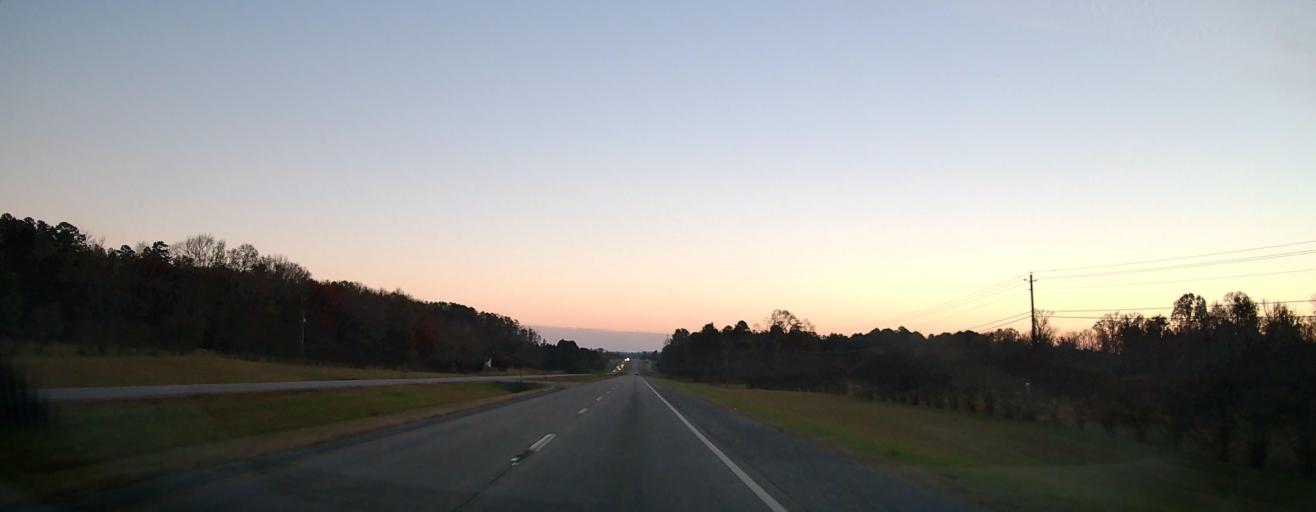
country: US
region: Alabama
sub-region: Calhoun County
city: Alexandria
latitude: 33.8365
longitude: -85.9140
